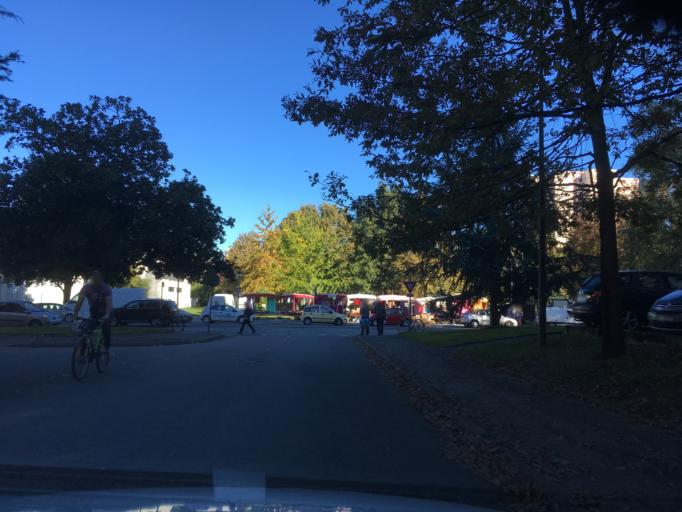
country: FR
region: Aquitaine
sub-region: Departement des Pyrenees-Atlantiques
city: Pau
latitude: 43.3076
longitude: -0.3588
